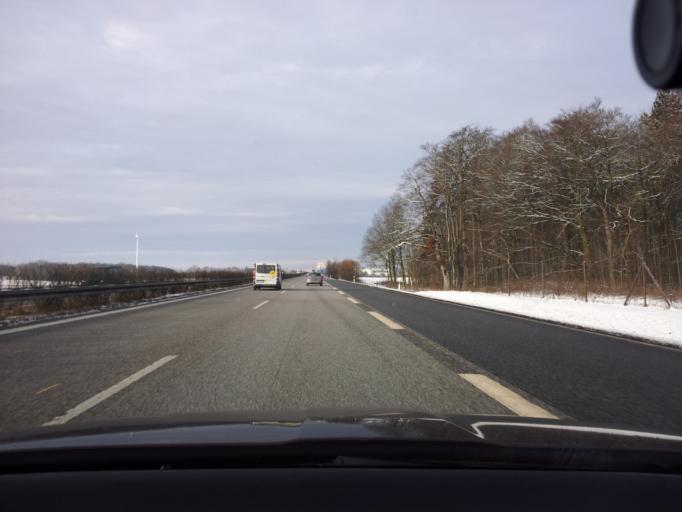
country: DE
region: Mecklenburg-Vorpommern
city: Wittenburg
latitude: 53.4957
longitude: 11.1239
